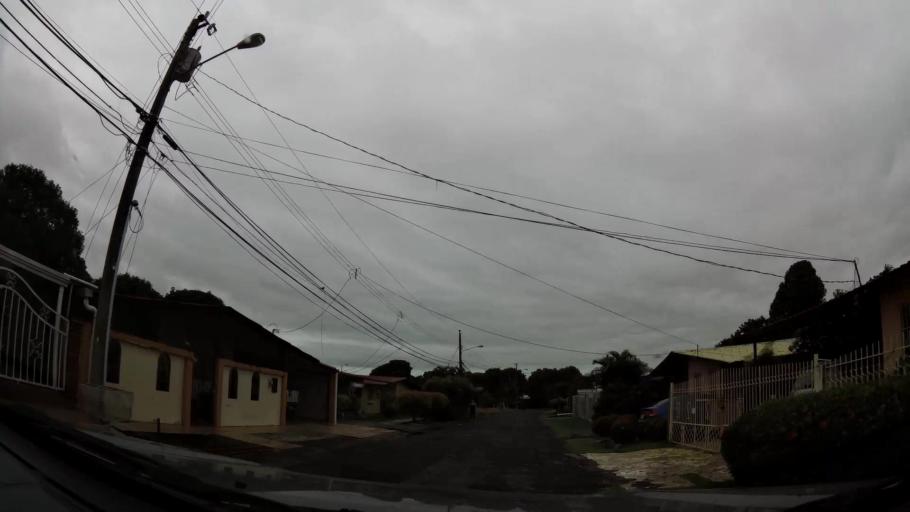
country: PA
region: Chiriqui
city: David
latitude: 8.4353
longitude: -82.4449
